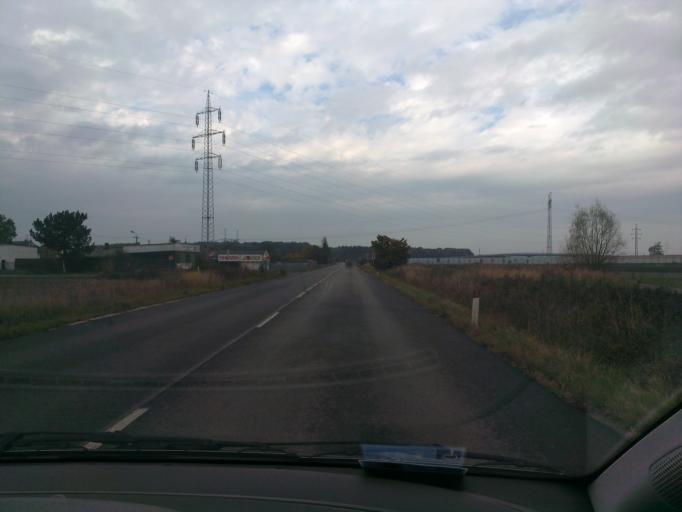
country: CZ
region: Zlin
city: Lesna
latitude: 49.5068
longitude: 17.9339
